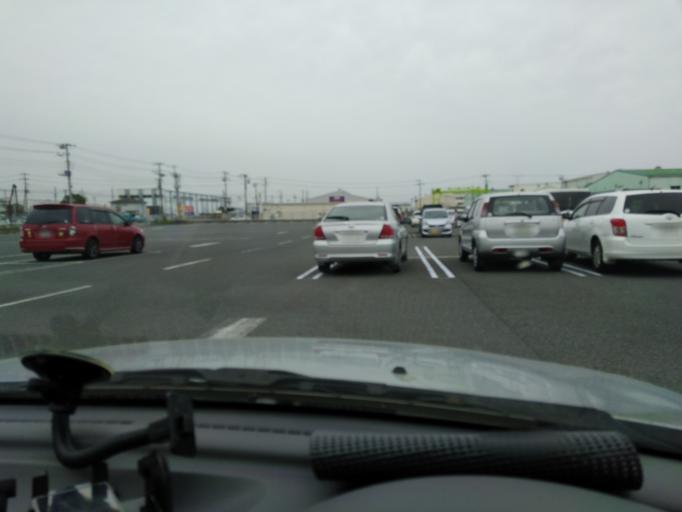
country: JP
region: Chiba
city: Ichihara
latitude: 35.4906
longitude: 140.0459
